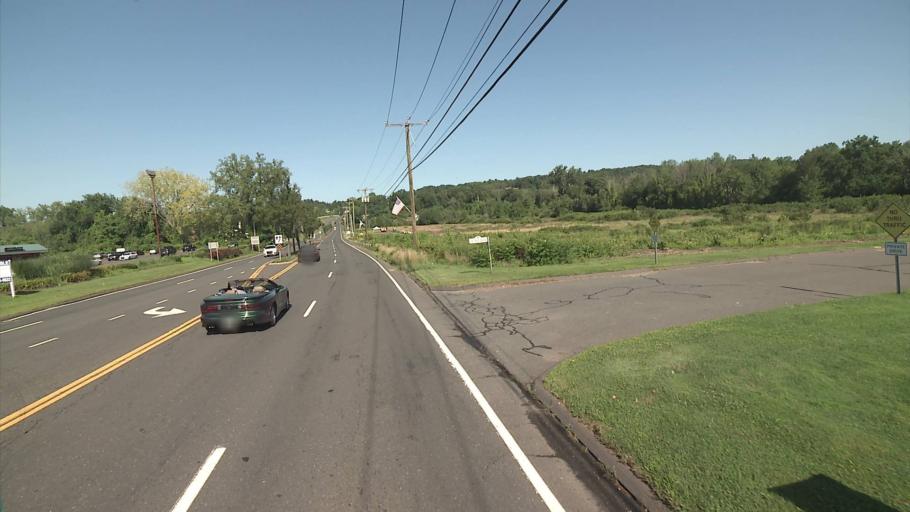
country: US
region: Connecticut
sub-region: Hartford County
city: Tariffville
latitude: 41.9435
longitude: -72.7273
